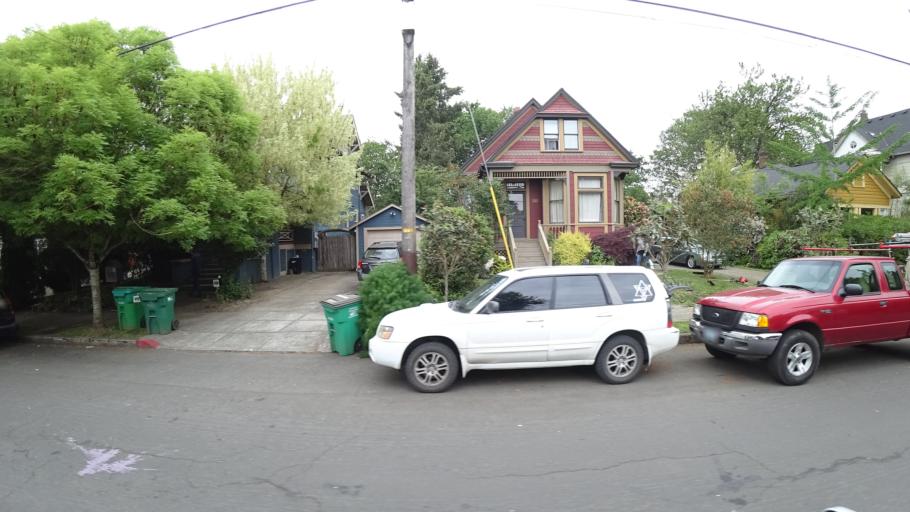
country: US
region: Oregon
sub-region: Multnomah County
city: Portland
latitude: 45.5430
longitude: -122.6602
